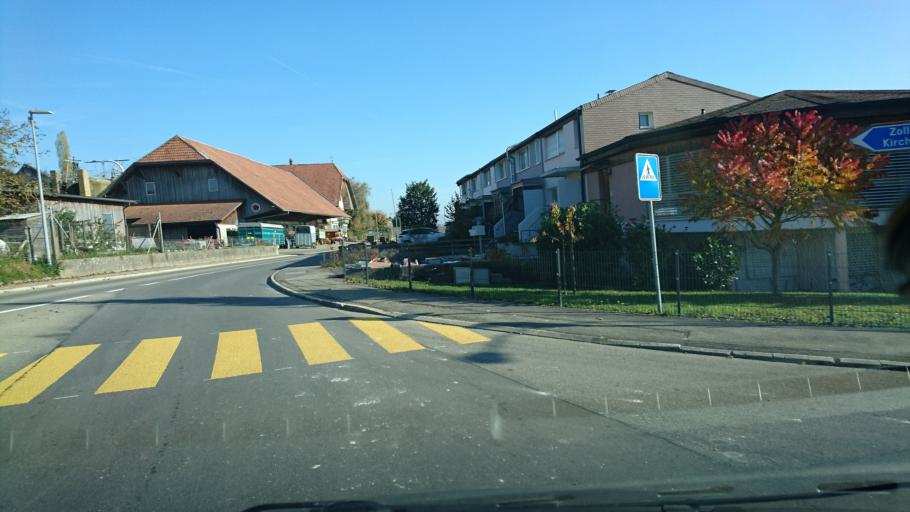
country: CH
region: Bern
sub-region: Bern-Mittelland District
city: Kirchlindach
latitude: 46.9952
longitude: 7.3983
